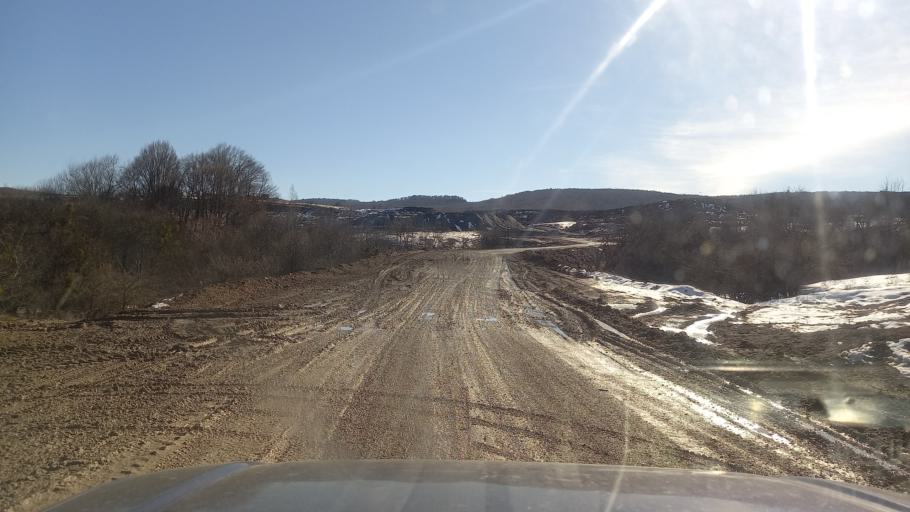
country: RU
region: Adygeya
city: Kamennomostskiy
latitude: 44.2798
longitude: 40.3258
